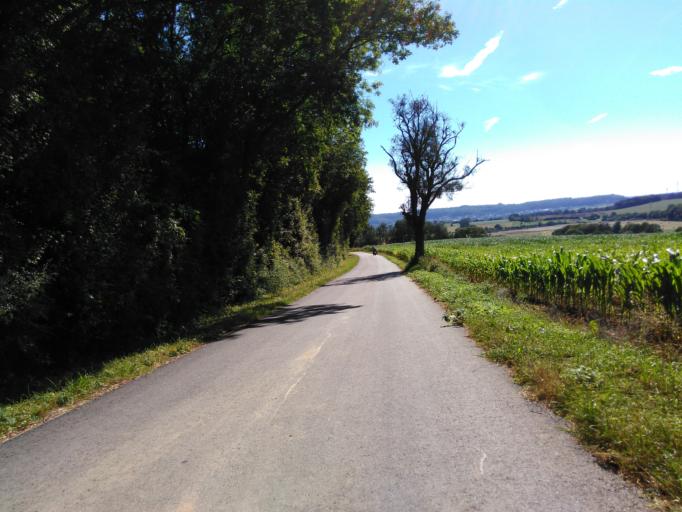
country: LU
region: Luxembourg
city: Schouweiler
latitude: 49.5574
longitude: 5.9540
